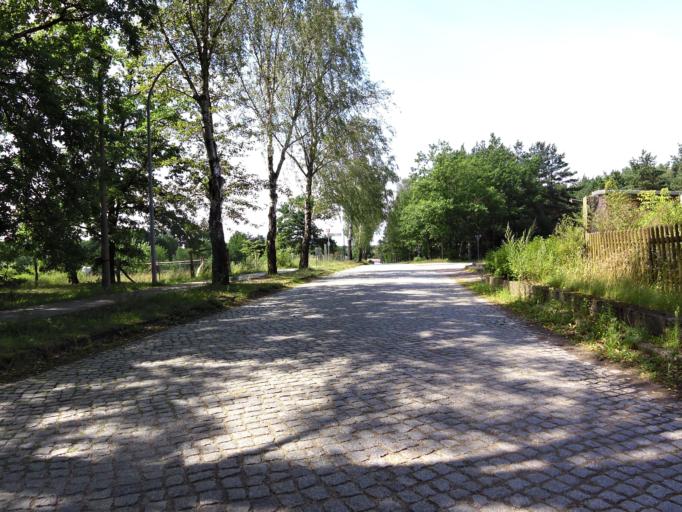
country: DE
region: Brandenburg
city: Furstenberg
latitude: 53.1945
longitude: 13.1532
